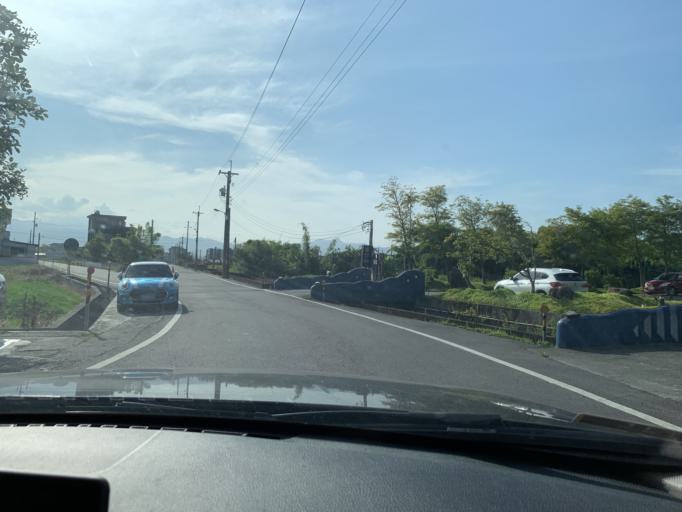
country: TW
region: Taiwan
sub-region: Yilan
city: Yilan
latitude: 24.6789
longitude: 121.8081
